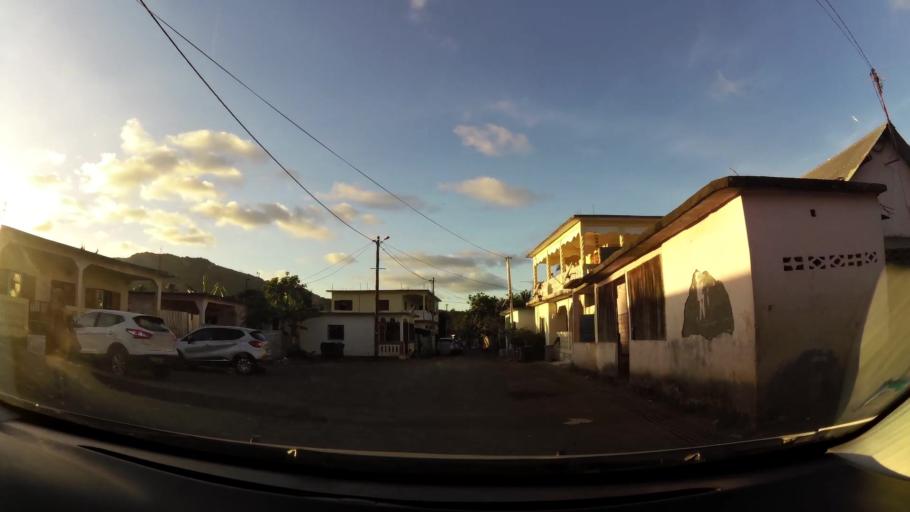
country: YT
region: Dembeni
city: Dembeni
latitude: -12.8441
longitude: 45.1909
